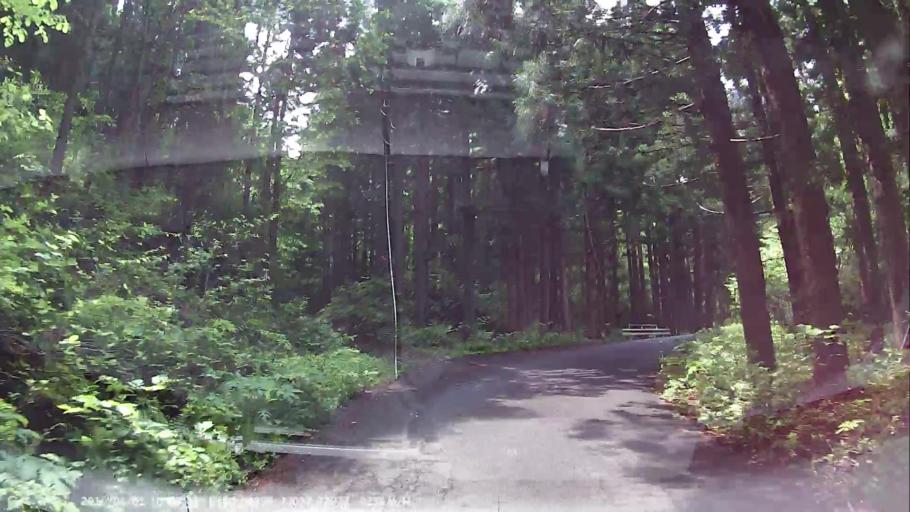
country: JP
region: Fukushima
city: Inawashiro
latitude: 37.3297
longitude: 140.0840
